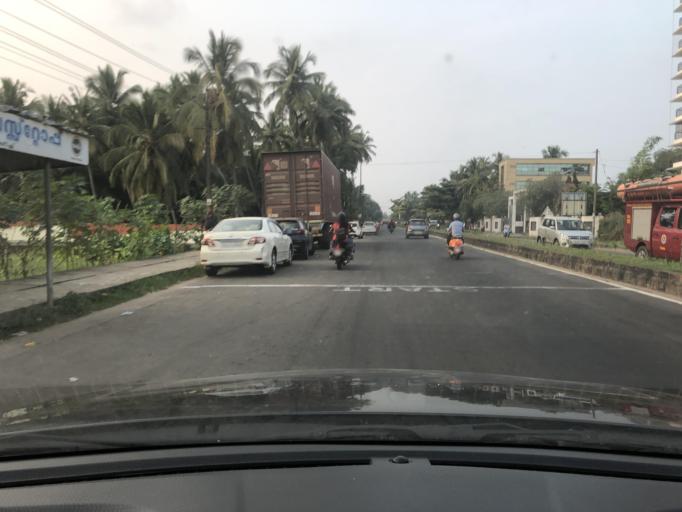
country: IN
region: Kerala
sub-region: Kozhikode
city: Kozhikode
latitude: 11.2913
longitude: 75.7585
